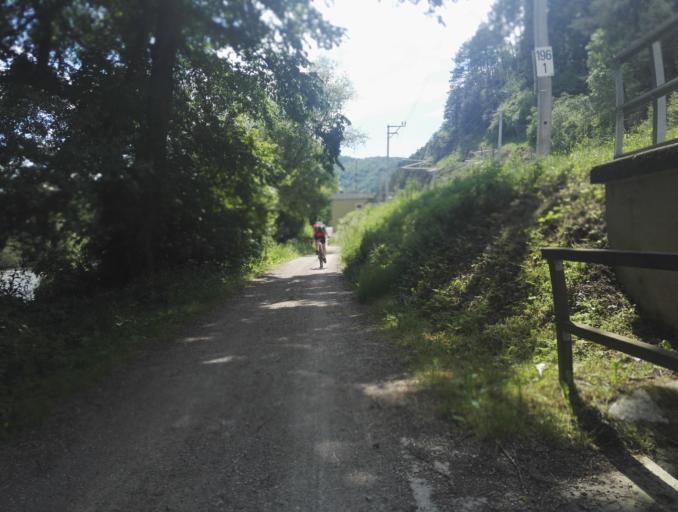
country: AT
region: Styria
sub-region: Politischer Bezirk Graz-Umgebung
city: Deutschfeistritz
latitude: 47.1664
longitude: 15.3188
